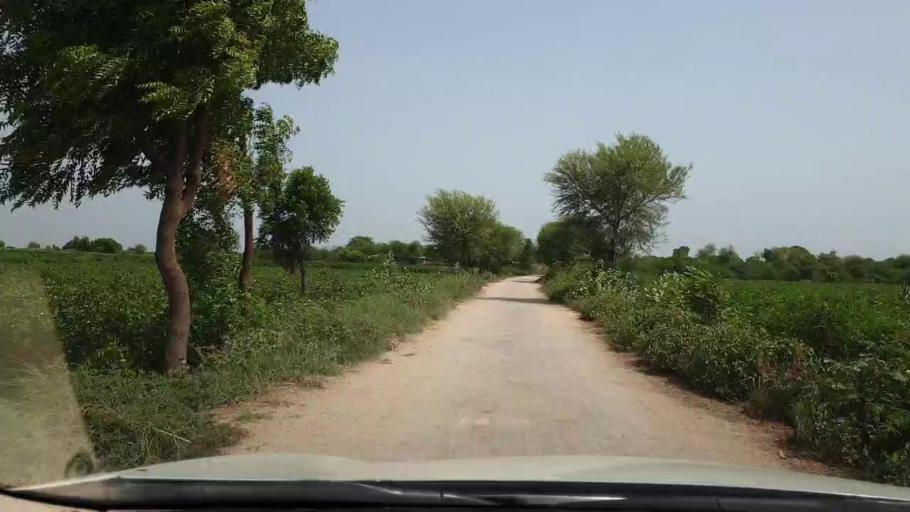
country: PK
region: Sindh
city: Tando Ghulam Ali
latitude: 25.2317
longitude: 68.9160
